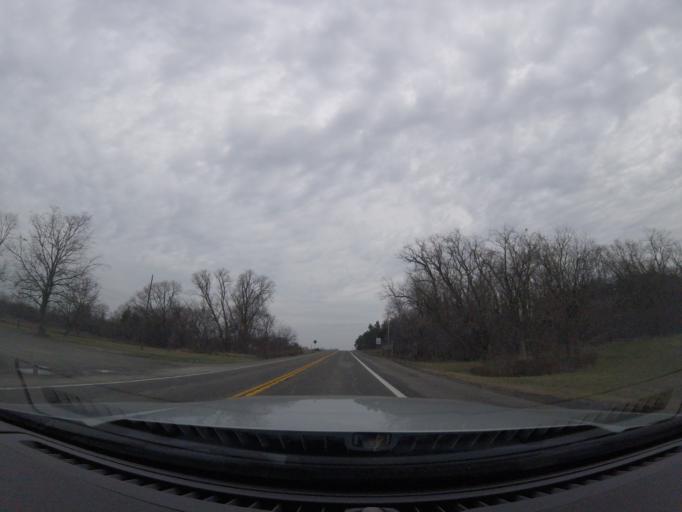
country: US
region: New York
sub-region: Yates County
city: Dundee
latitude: 42.5187
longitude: -76.9219
